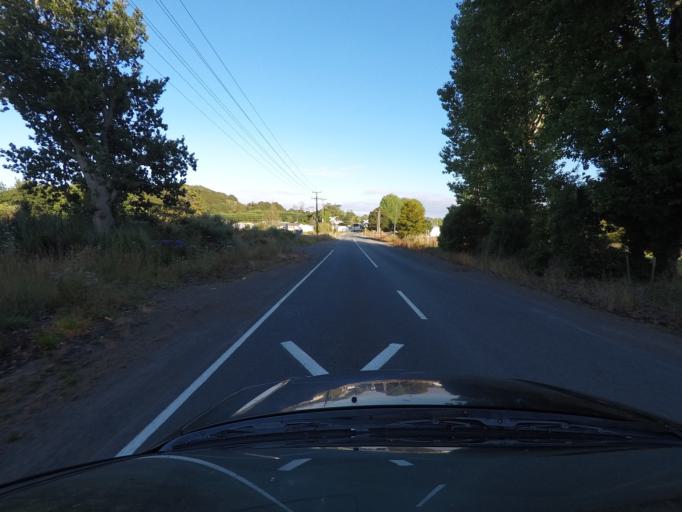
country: NZ
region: Northland
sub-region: Whangarei
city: Whangarei
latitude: -35.6425
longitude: 174.2993
